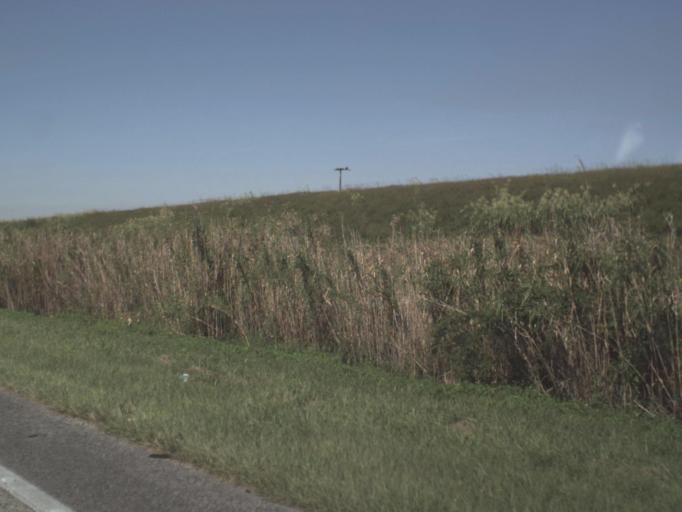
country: US
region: Florida
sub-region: Hendry County
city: Clewiston
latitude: 26.7509
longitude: -80.9022
